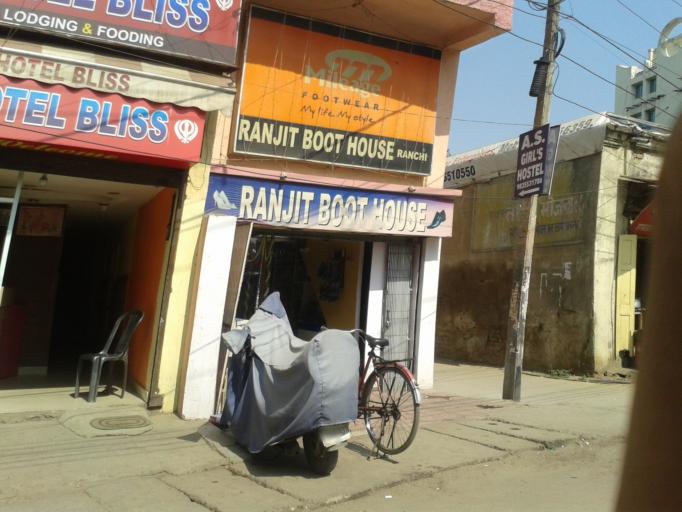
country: IN
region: Jharkhand
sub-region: Ranchi
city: Ranchi
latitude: 23.3720
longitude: 85.3368
